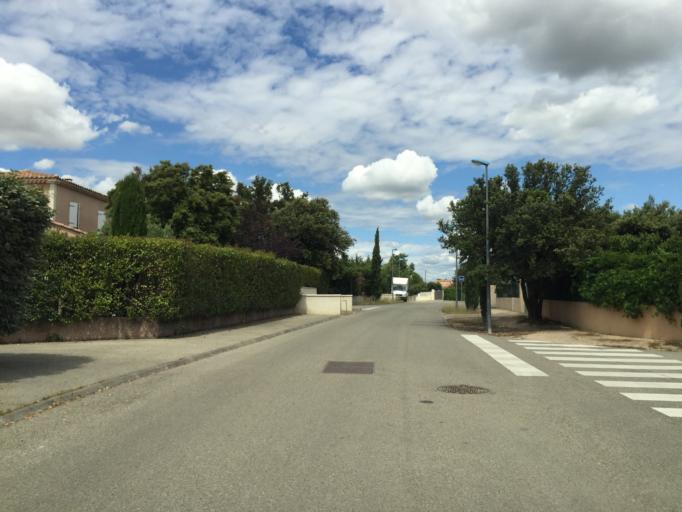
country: FR
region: Provence-Alpes-Cote d'Azur
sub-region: Departement du Vaucluse
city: Sorgues
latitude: 44.0194
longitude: 4.8578
